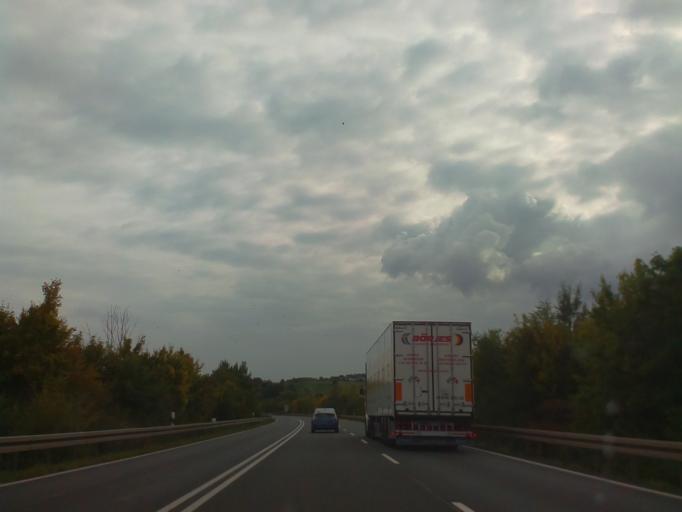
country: DE
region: Hesse
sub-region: Regierungsbezirk Kassel
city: Hunfeld
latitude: 50.6853
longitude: 9.7528
